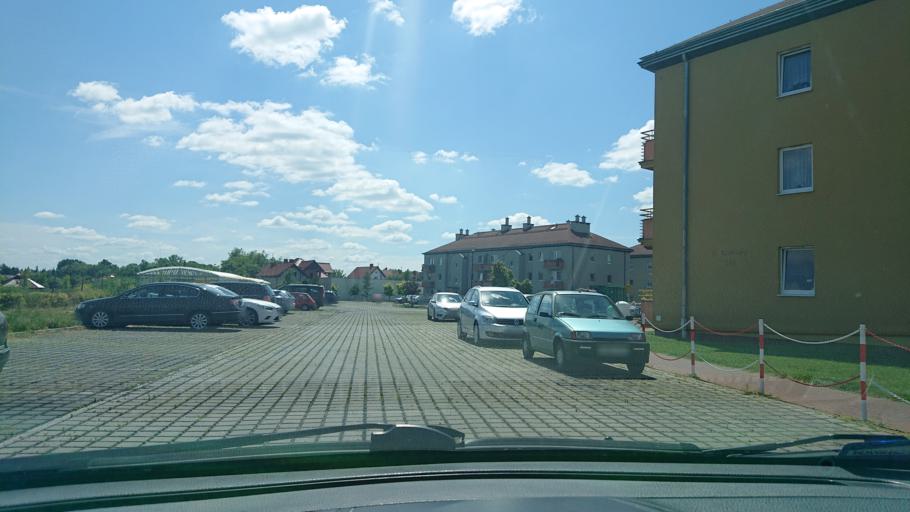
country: PL
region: Greater Poland Voivodeship
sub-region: Powiat gnieznienski
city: Gniezno
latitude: 52.5224
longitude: 17.6149
